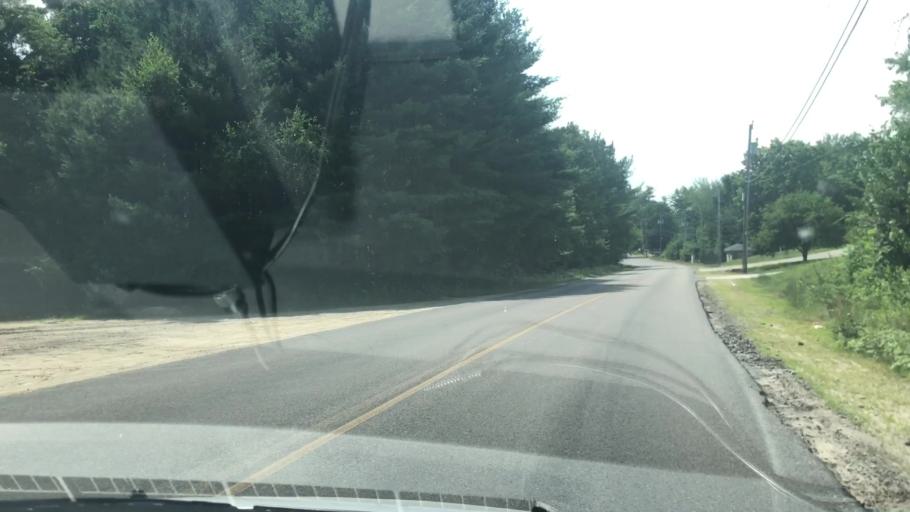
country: US
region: New Hampshire
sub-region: Hillsborough County
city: Milford
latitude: 42.8155
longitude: -71.6329
